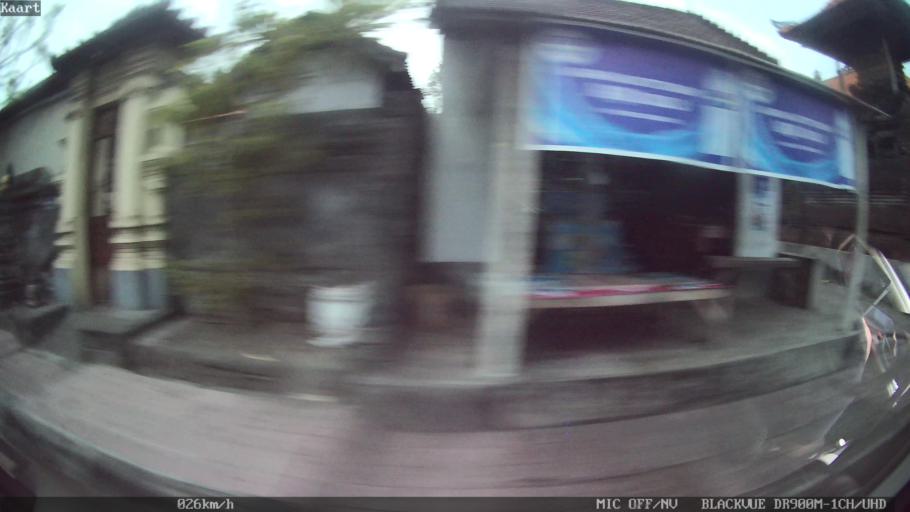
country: ID
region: Bali
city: Banjar Pasekan
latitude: -8.6301
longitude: 115.2845
